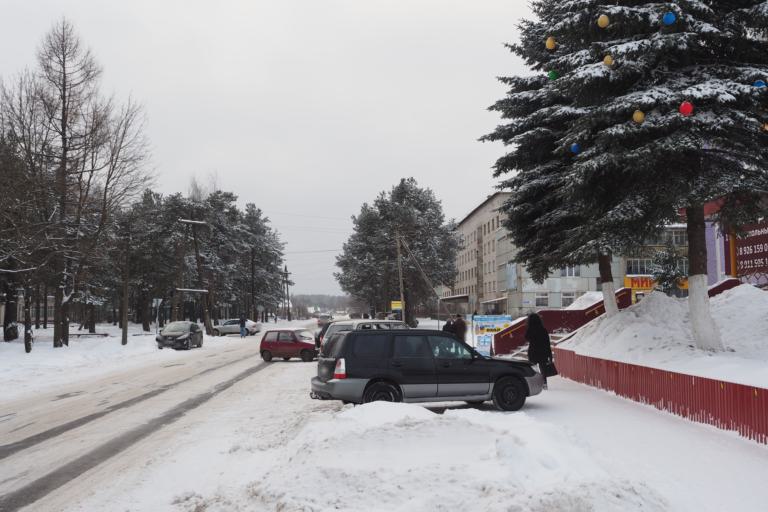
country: RU
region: Tverskaya
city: Ves'yegonsk
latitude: 58.6565
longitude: 37.2579
